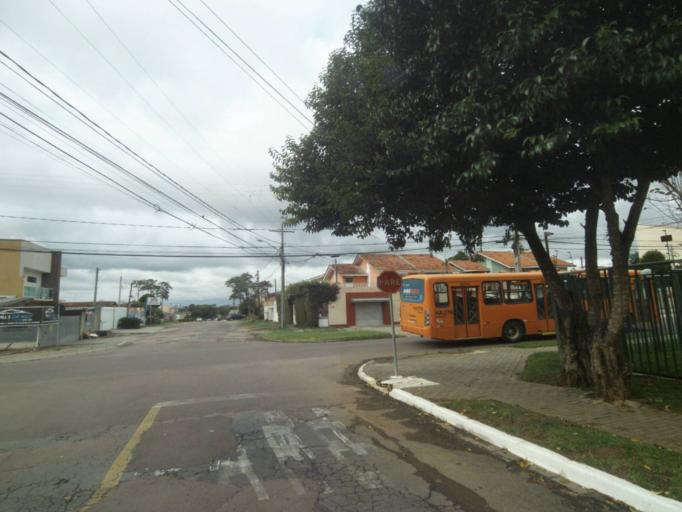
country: BR
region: Parana
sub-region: Curitiba
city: Curitiba
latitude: -25.4943
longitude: -49.3084
